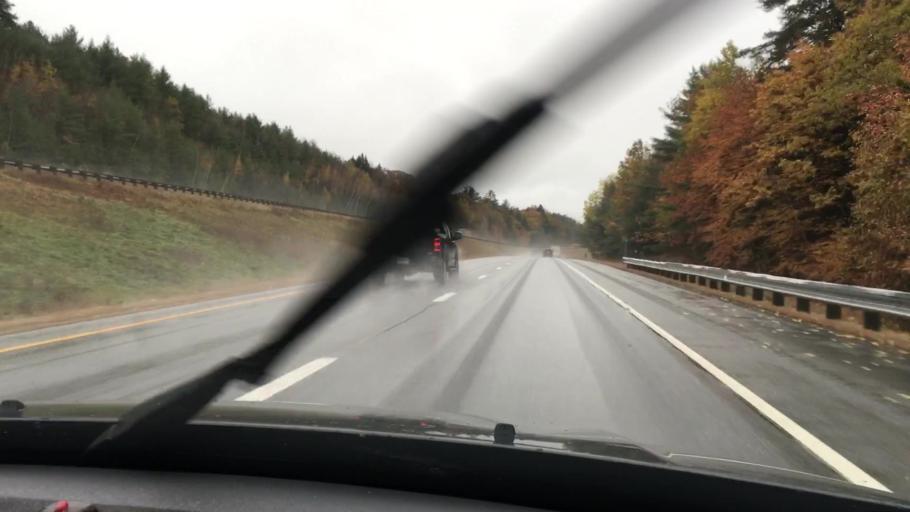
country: US
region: New Hampshire
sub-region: Grafton County
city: Ashland
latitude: 43.6400
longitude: -71.6491
